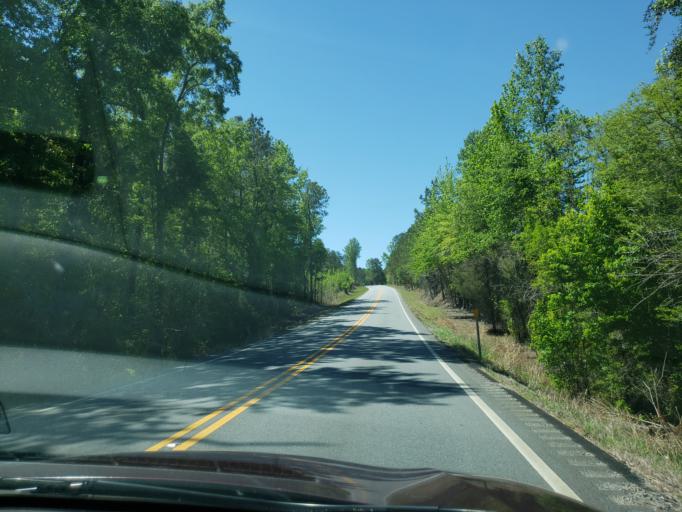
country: US
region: Alabama
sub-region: Tallapoosa County
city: Dadeville
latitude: 32.6775
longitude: -85.7892
